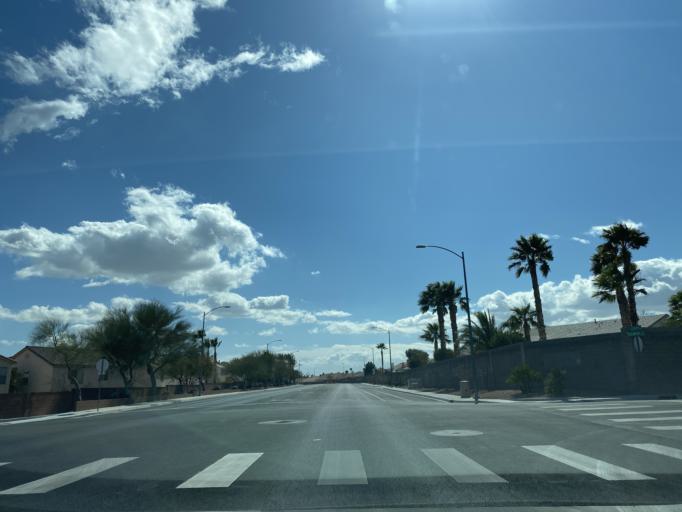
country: US
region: Nevada
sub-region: Clark County
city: Summerlin South
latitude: 36.2299
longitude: -115.3065
